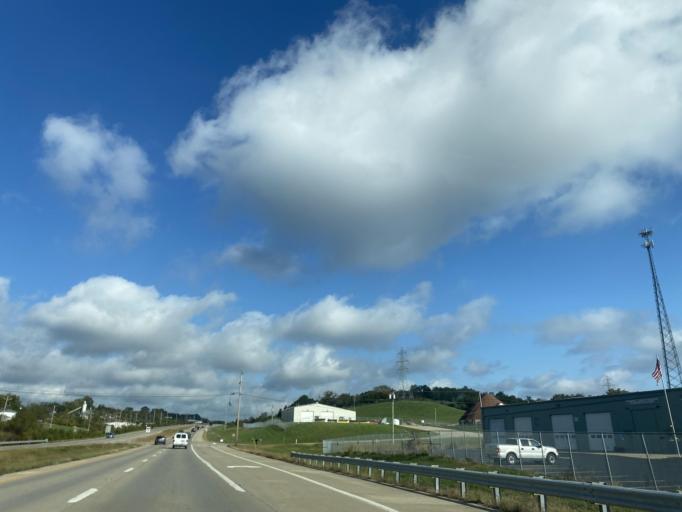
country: US
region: Kentucky
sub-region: Campbell County
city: Claryville
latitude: 38.9279
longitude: -84.3931
